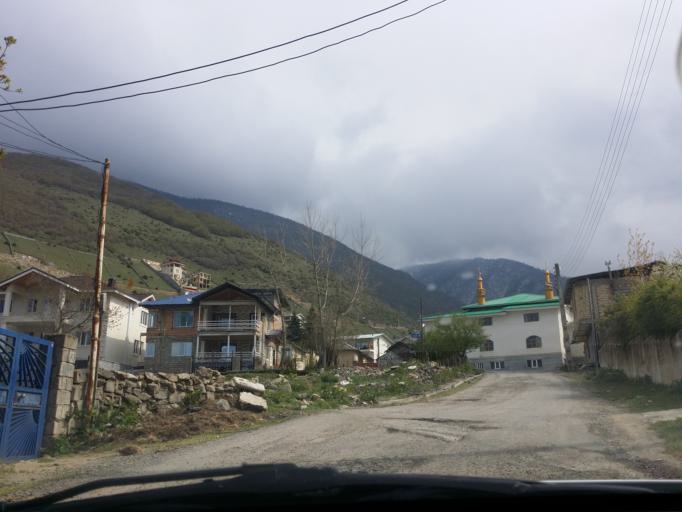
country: IR
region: Mazandaran
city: `Abbasabad
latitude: 36.4834
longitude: 51.1388
